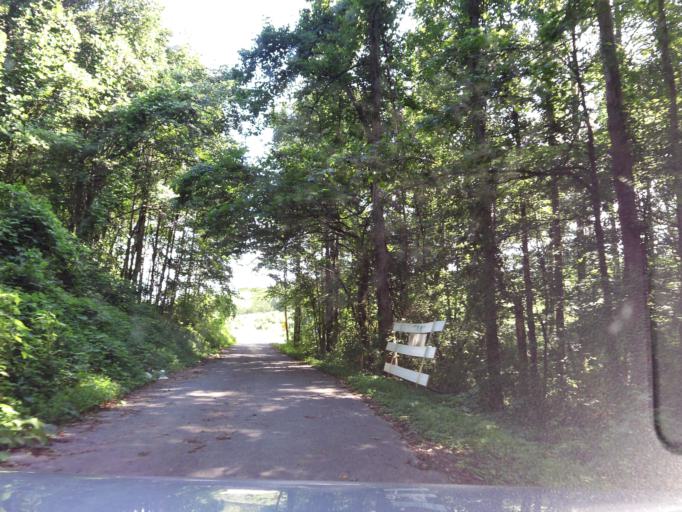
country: US
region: Tennessee
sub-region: Union County
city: Condon
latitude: 36.1351
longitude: -83.9121
